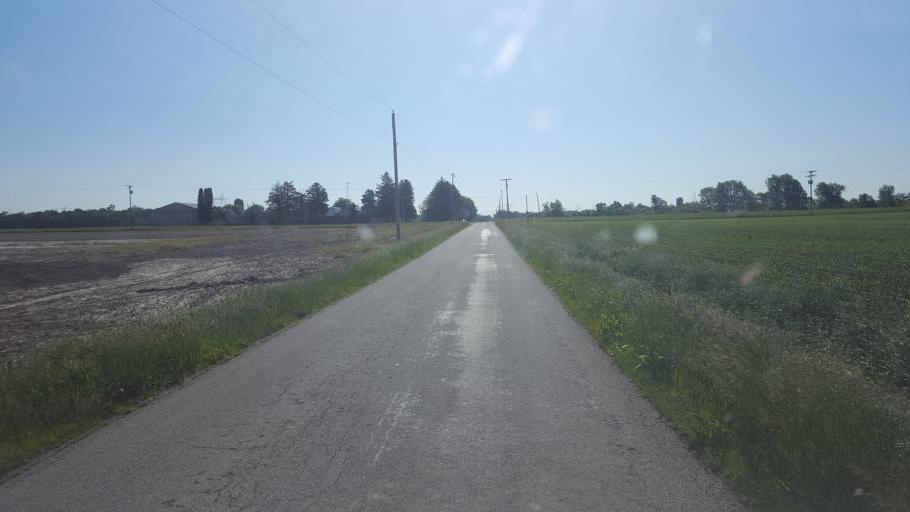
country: US
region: Ohio
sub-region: Crawford County
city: Bucyrus
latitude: 40.7399
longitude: -82.9389
